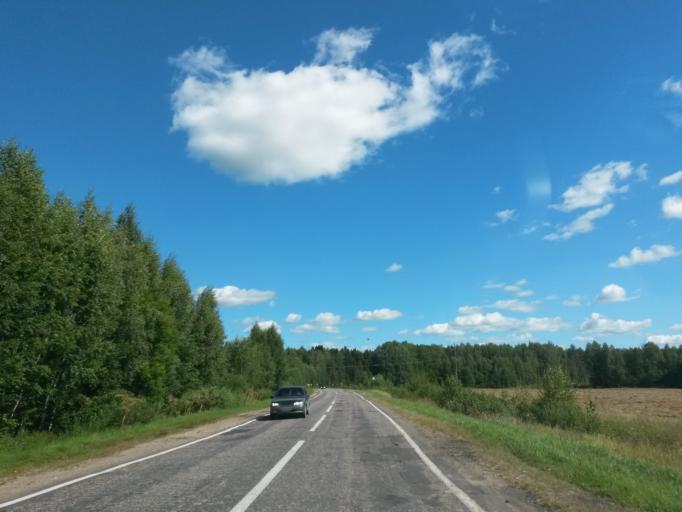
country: RU
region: Jaroslavl
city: Konstantinovskiy
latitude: 57.8046
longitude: 39.7723
